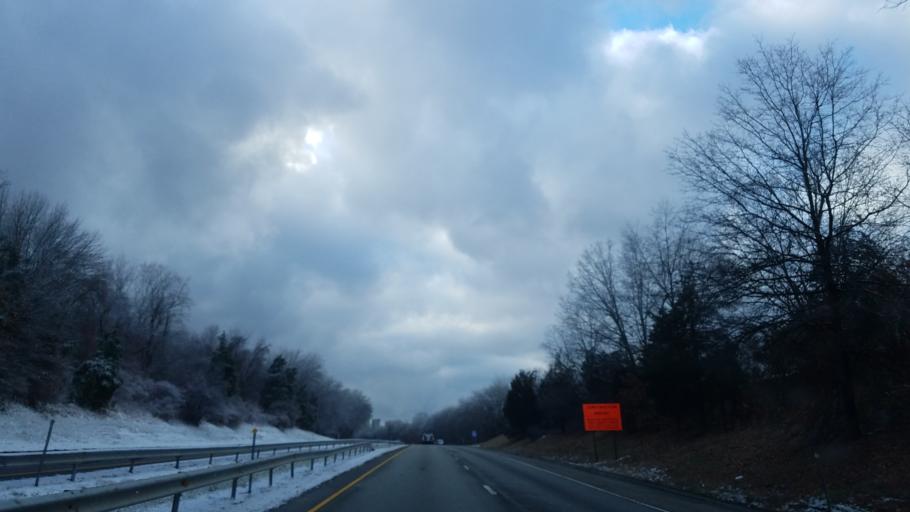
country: US
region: Connecticut
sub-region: New London County
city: Baltic
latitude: 41.5847
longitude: -72.0585
